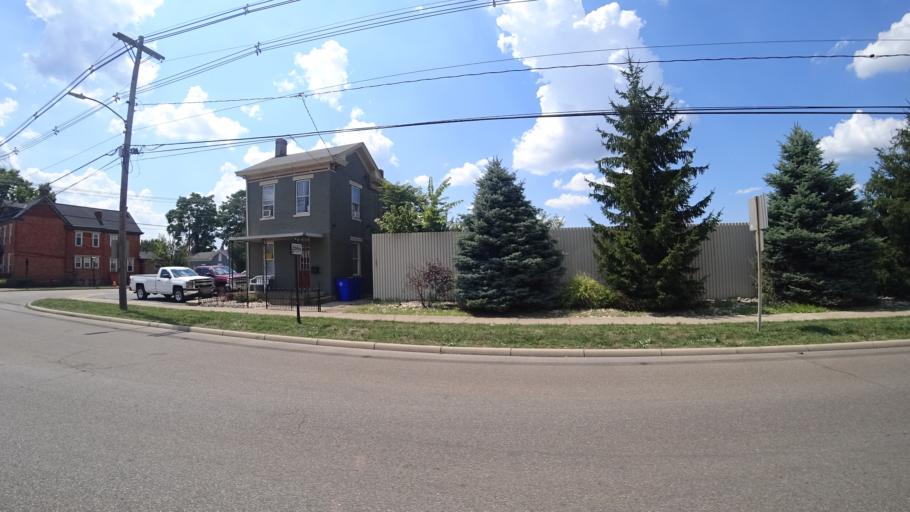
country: US
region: Ohio
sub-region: Butler County
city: Hamilton
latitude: 39.4055
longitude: -84.5573
